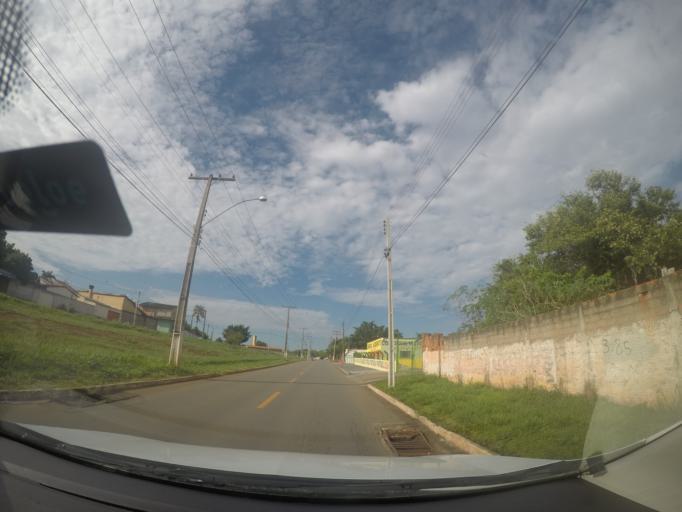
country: BR
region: Goias
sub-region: Goiania
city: Goiania
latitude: -16.6894
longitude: -49.1896
